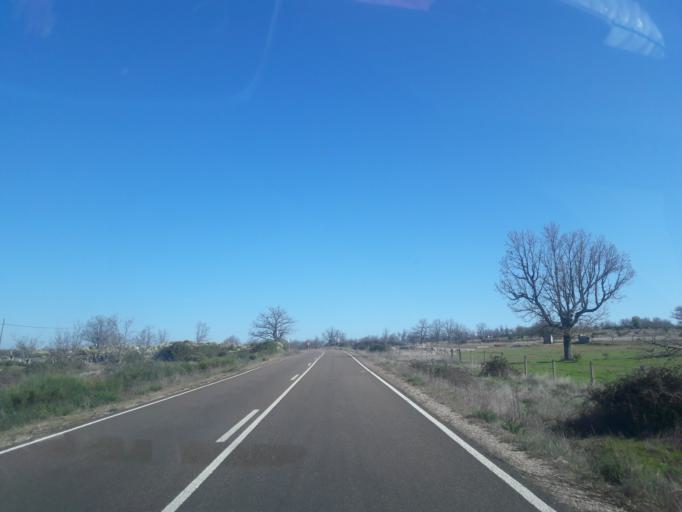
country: ES
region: Castille and Leon
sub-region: Provincia de Salamanca
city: Cabeza del Caballo
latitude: 41.1165
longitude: -6.5562
